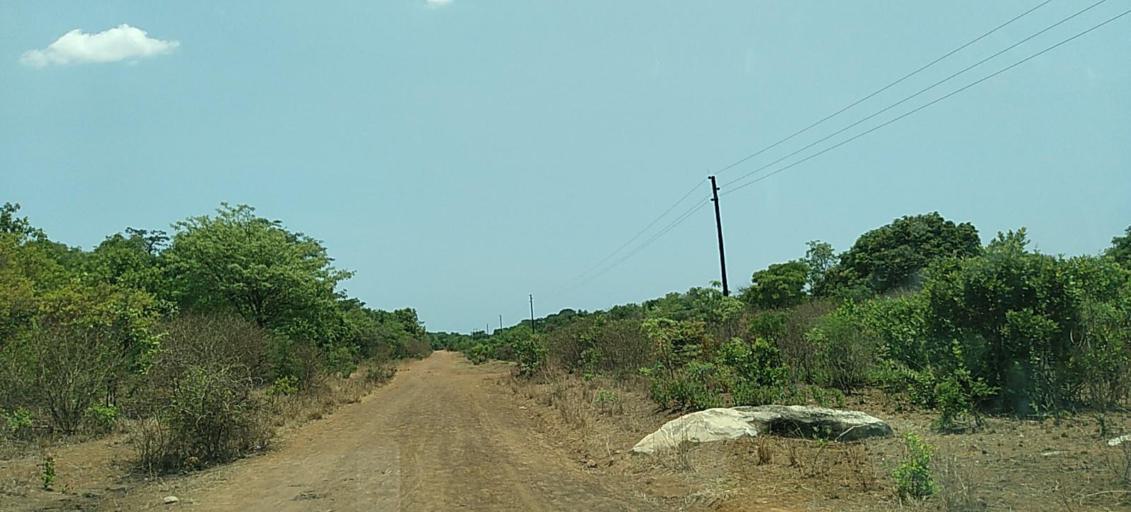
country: ZM
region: Copperbelt
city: Mpongwe
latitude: -13.8269
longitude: 27.8393
